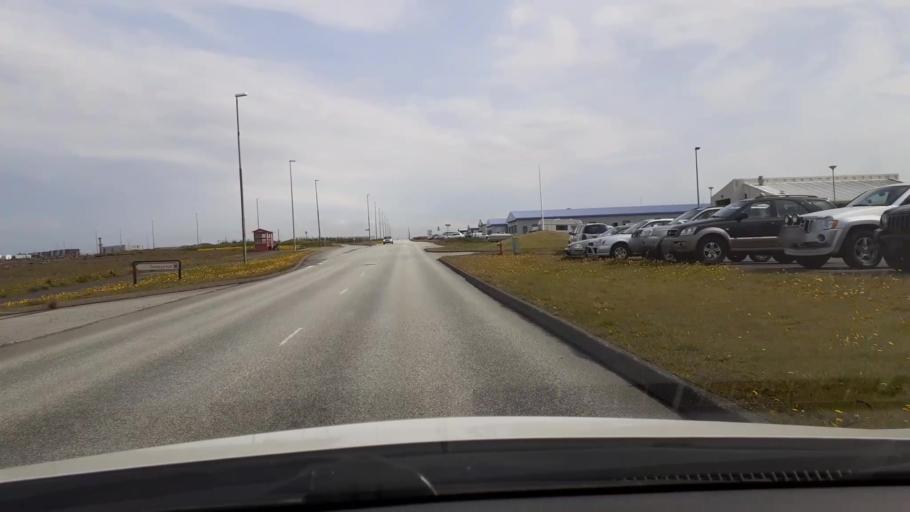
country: IS
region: Southern Peninsula
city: Reykjanesbaer
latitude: 63.9723
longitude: -22.5320
